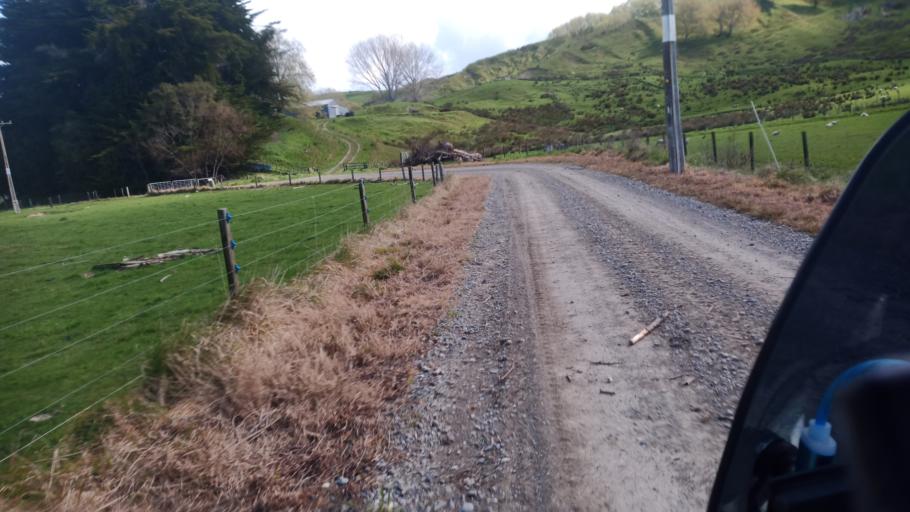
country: NZ
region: Gisborne
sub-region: Gisborne District
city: Gisborne
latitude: -38.3868
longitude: 178.2609
